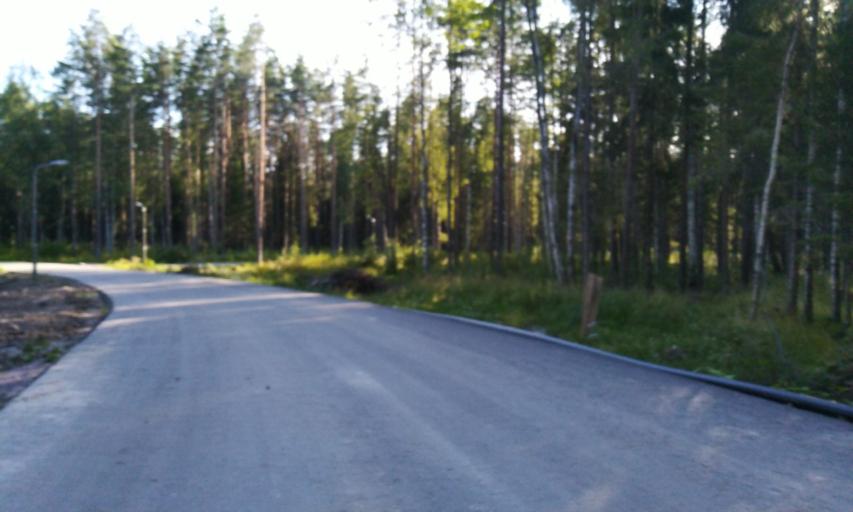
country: RU
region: Leningrad
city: Toksovo
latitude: 60.1330
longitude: 30.4561
